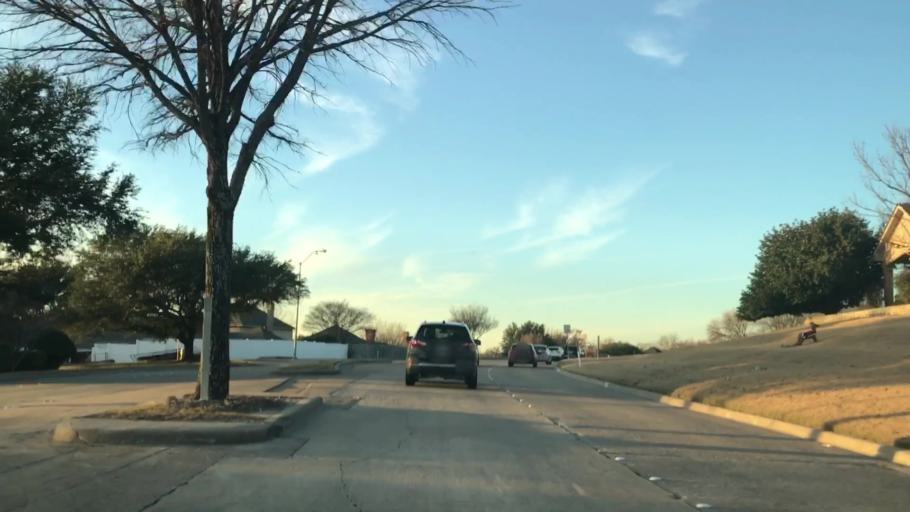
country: US
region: Texas
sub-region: Rockwall County
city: Rockwall
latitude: 32.9351
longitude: -96.4767
